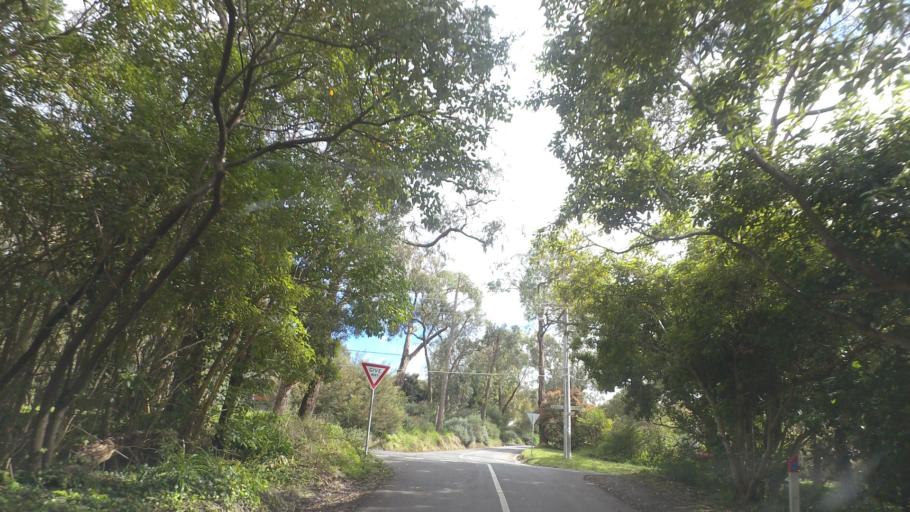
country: AU
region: Victoria
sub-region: Maroondah
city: Croydon South
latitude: -37.8046
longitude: 145.2616
